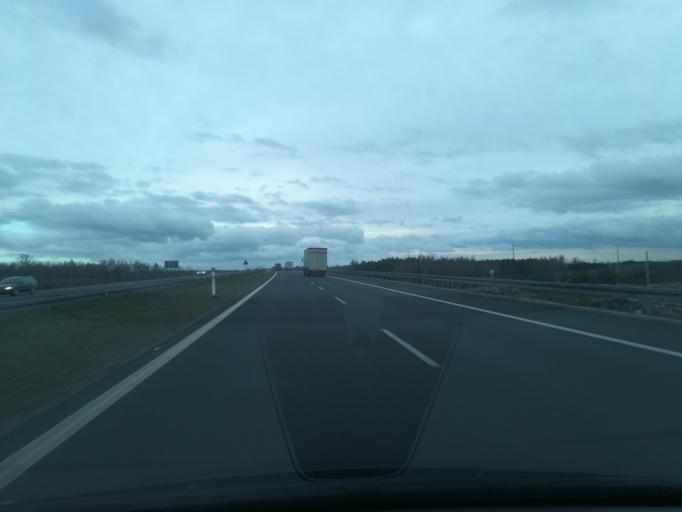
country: PL
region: Lodz Voivodeship
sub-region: Powiat kutnowski
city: Strzelce
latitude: 52.3160
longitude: 19.3625
